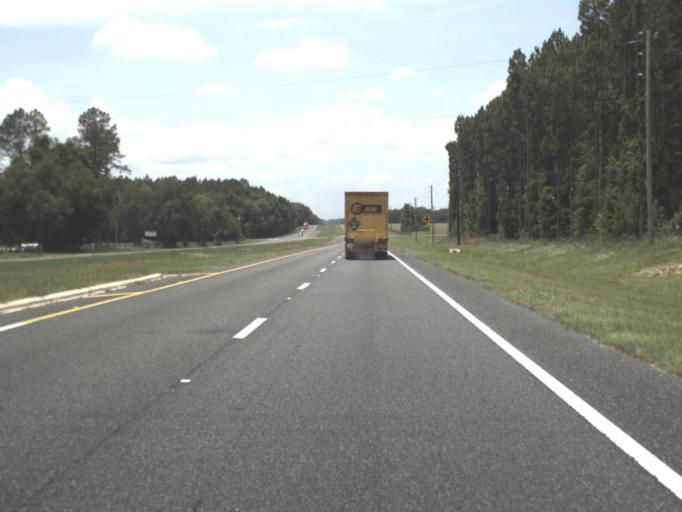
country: US
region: Florida
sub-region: Alachua County
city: Newberry
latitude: 29.6548
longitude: -82.5531
